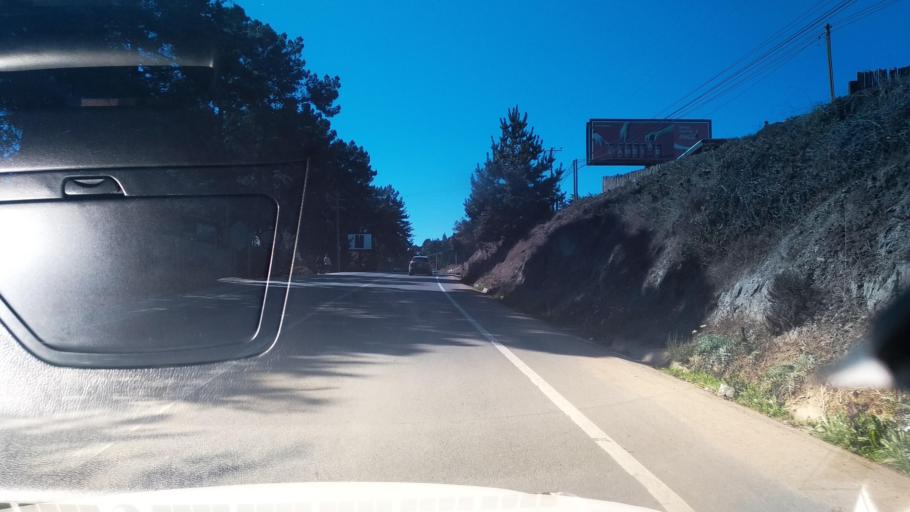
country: CL
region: O'Higgins
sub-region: Provincia de Colchagua
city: Santa Cruz
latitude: -34.4283
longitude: -72.0318
